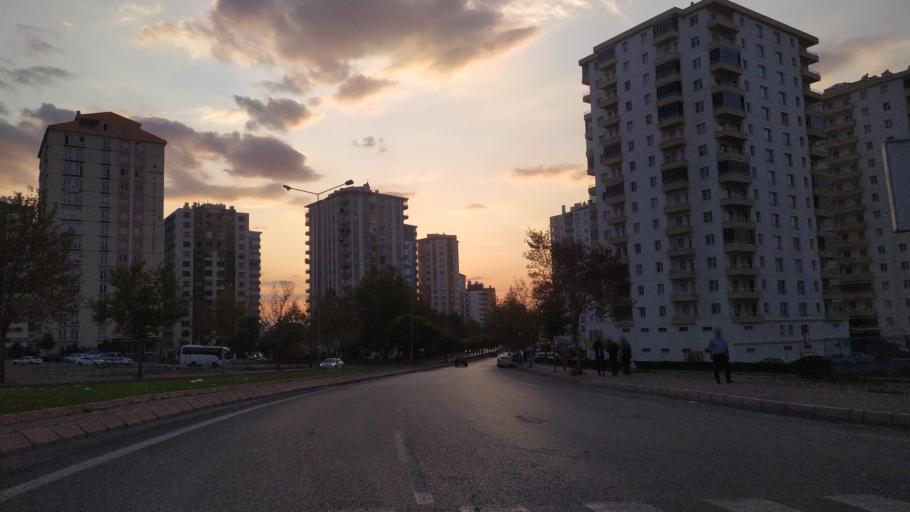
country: TR
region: Kayseri
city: Talas
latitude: 38.7086
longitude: 35.5605
